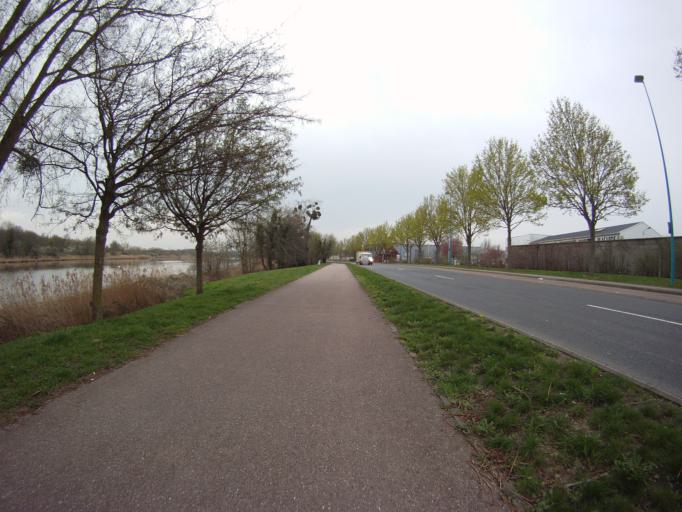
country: FR
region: Lorraine
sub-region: Departement de Meurthe-et-Moselle
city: Tomblaine
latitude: 48.6857
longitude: 6.2060
